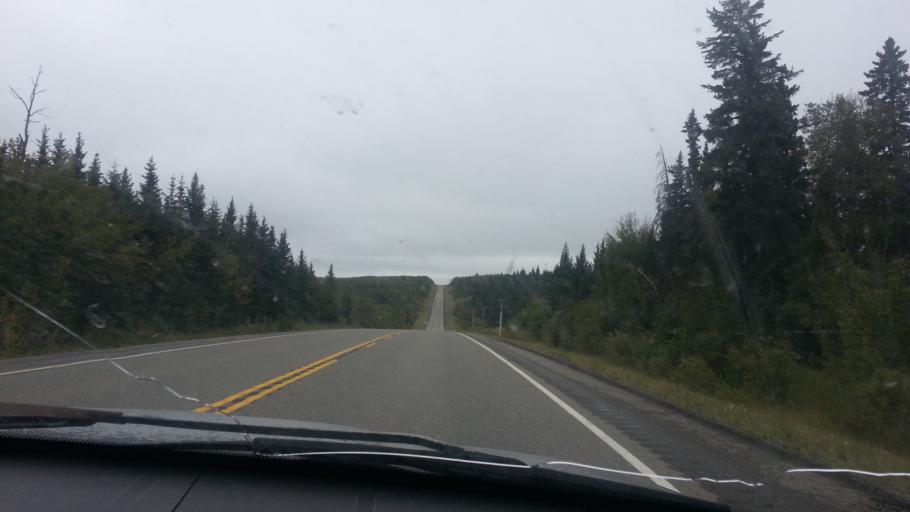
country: CA
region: Alberta
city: Cochrane
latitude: 51.0995
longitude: -114.6993
